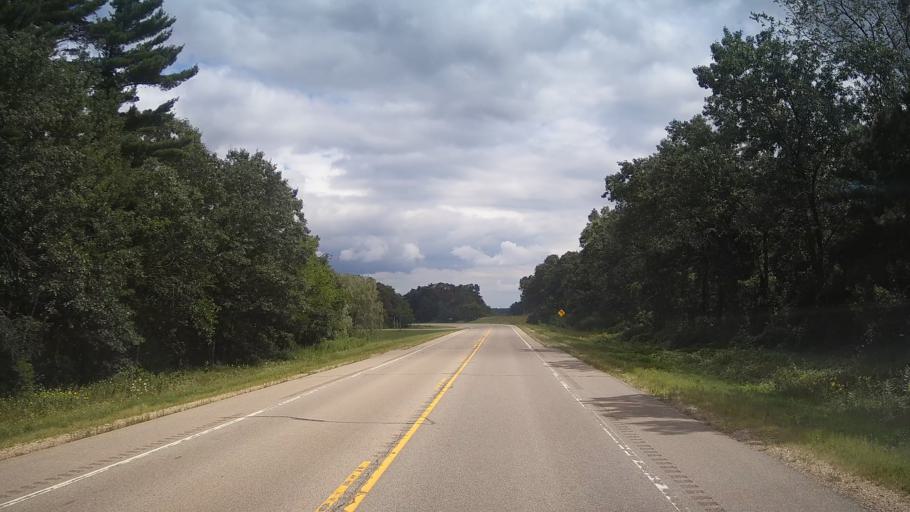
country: US
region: Wisconsin
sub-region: Marquette County
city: Westfield
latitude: 44.0218
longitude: -89.5491
